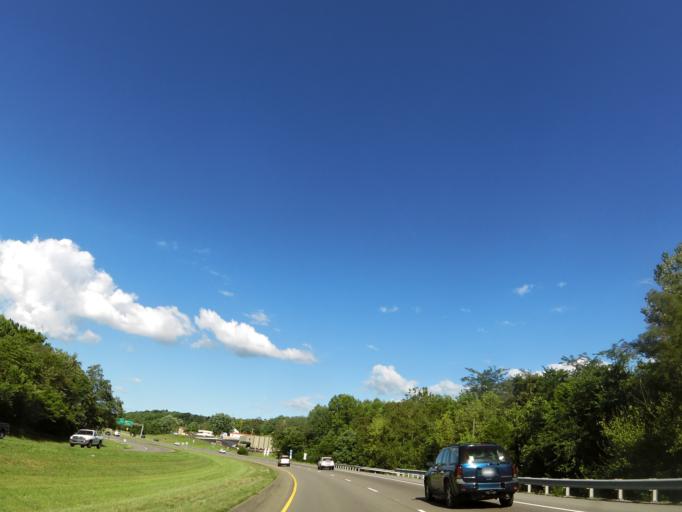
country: US
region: Tennessee
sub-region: Greene County
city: Greeneville
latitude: 36.1673
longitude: -82.8657
